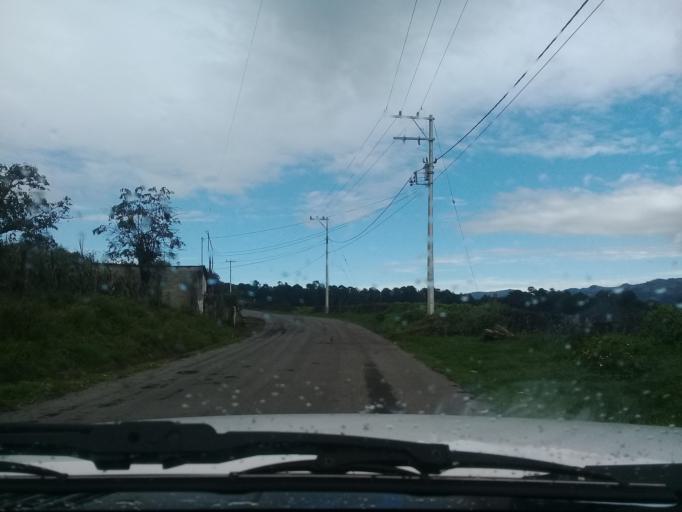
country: MX
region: Veracruz
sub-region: Acajete
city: La Joya
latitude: 19.6124
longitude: -97.0050
